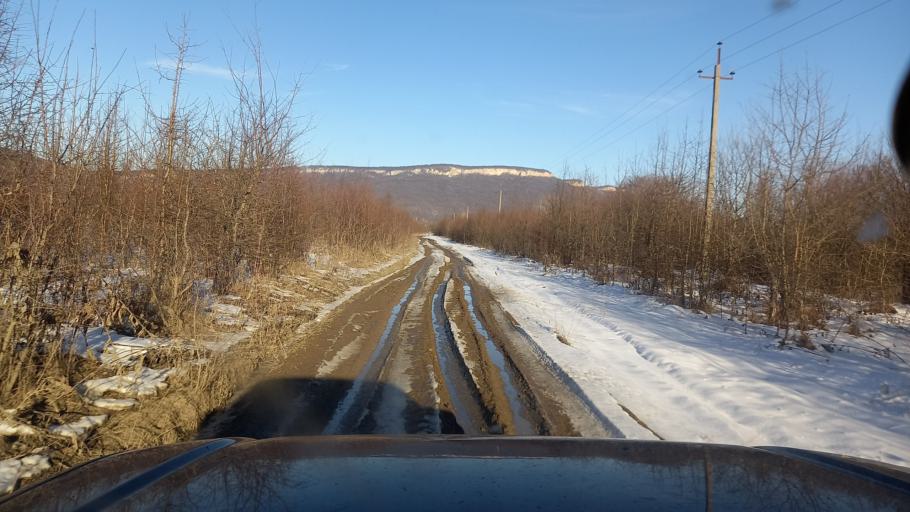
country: RU
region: Adygeya
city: Kamennomostskiy
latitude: 44.2126
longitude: 40.1682
